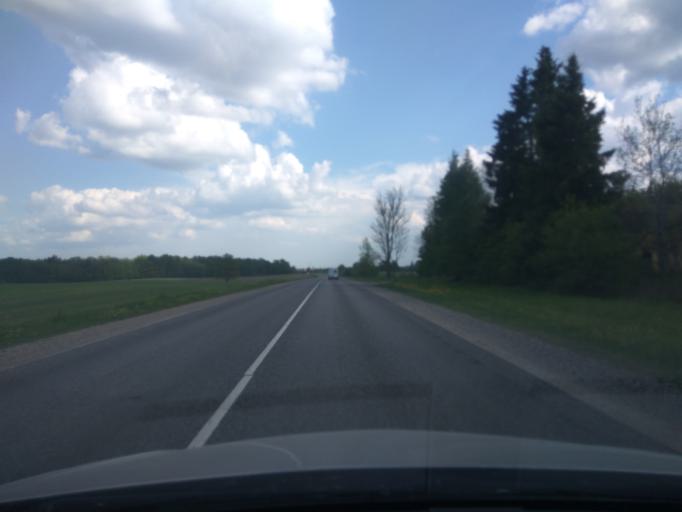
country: LV
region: Kuldigas Rajons
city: Kuldiga
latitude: 56.9901
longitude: 21.9158
